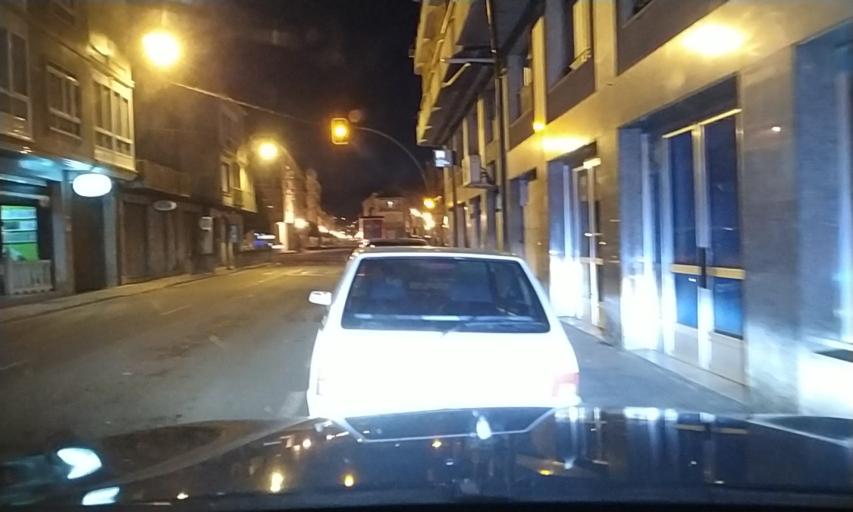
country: ES
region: Galicia
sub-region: Provincia de Ourense
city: Verin
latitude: 41.9411
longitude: -7.4330
